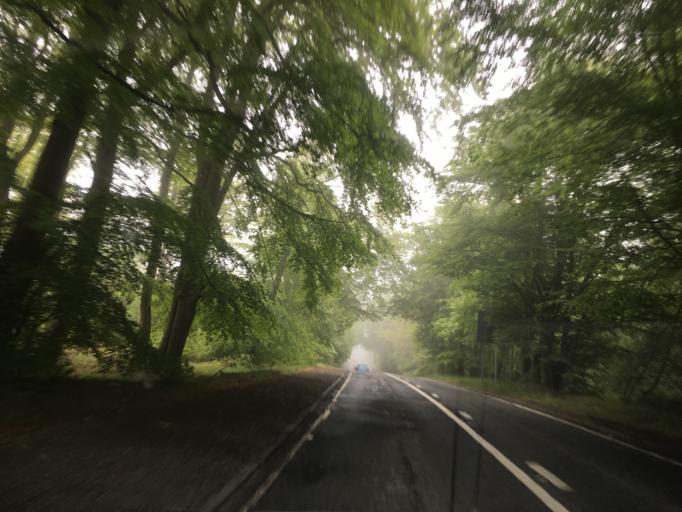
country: GB
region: Scotland
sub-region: Midlothian
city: Penicuik
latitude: 55.8181
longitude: -3.2021
